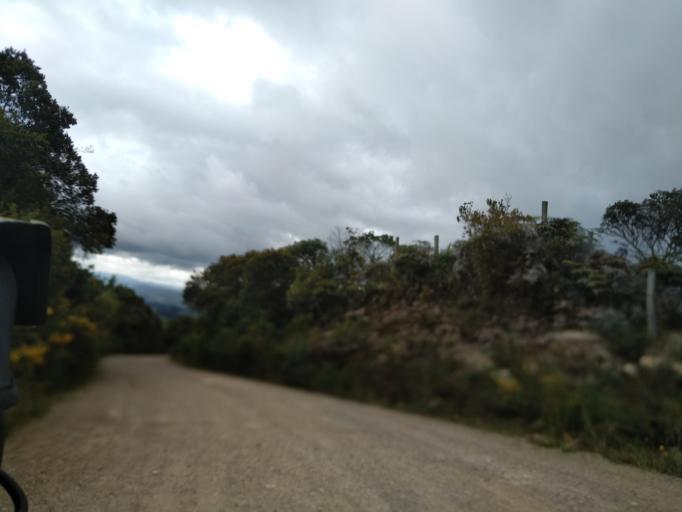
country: CO
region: Boyaca
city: Sotaquira
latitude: 5.7529
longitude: -73.2942
